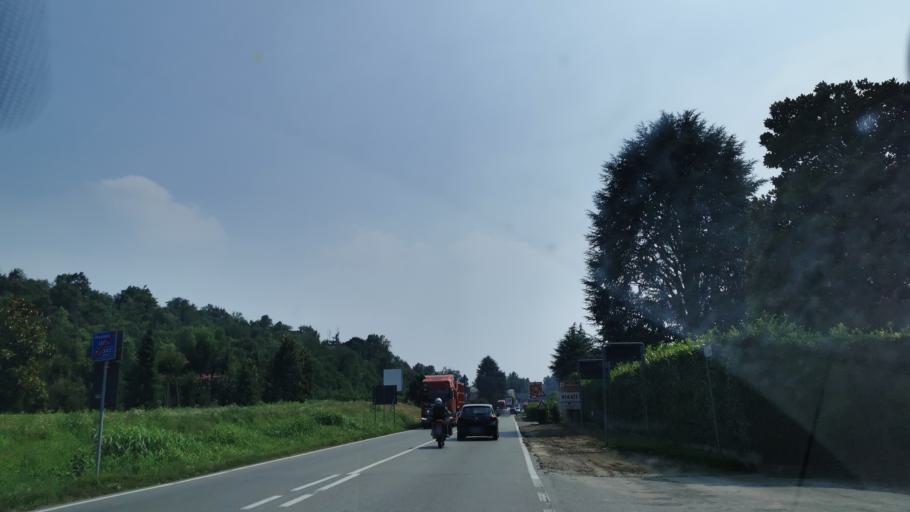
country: IT
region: Lombardy
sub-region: Provincia di Lecco
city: Calco
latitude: 45.7167
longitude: 9.4081
